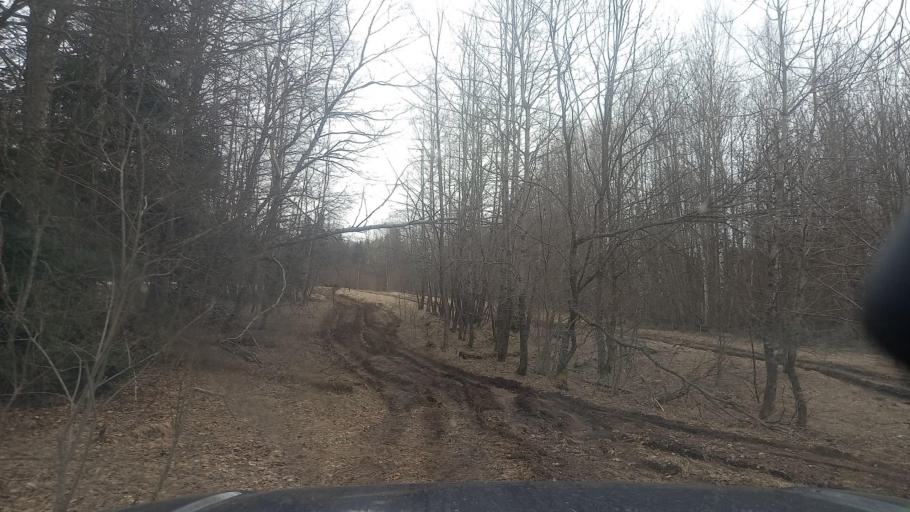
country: RU
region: Adygeya
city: Kamennomostskiy
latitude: 44.1666
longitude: 40.0245
